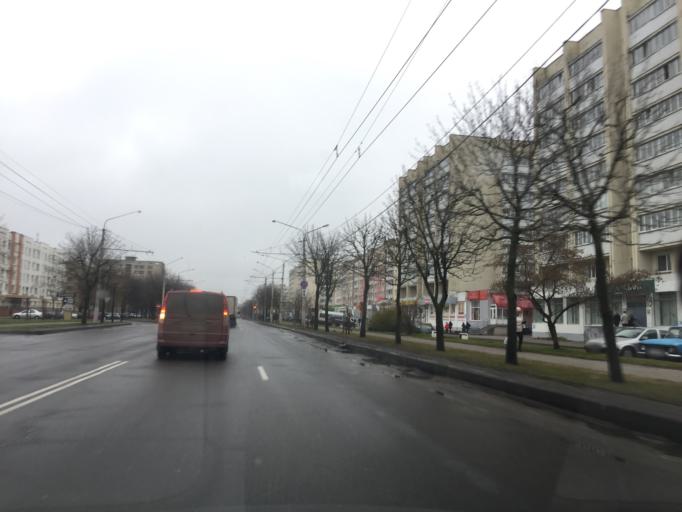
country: BY
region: Mogilev
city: Mahilyow
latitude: 53.8712
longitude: 30.3480
